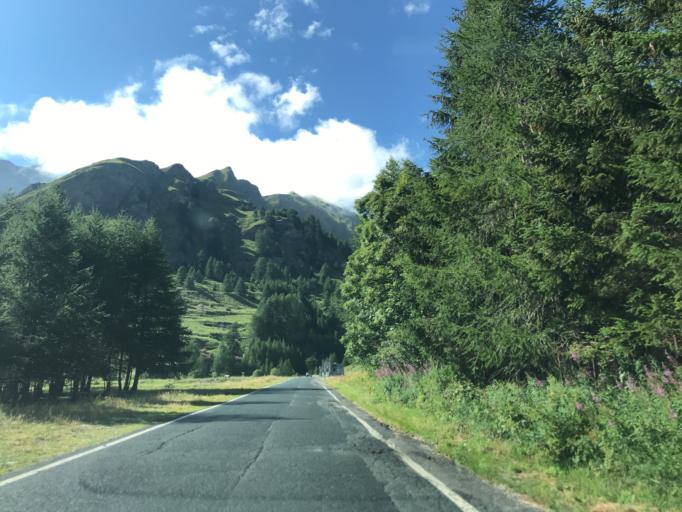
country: IT
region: Piedmont
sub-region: Provincia di Cuneo
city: Pontechianale
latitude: 44.6515
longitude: 6.9936
